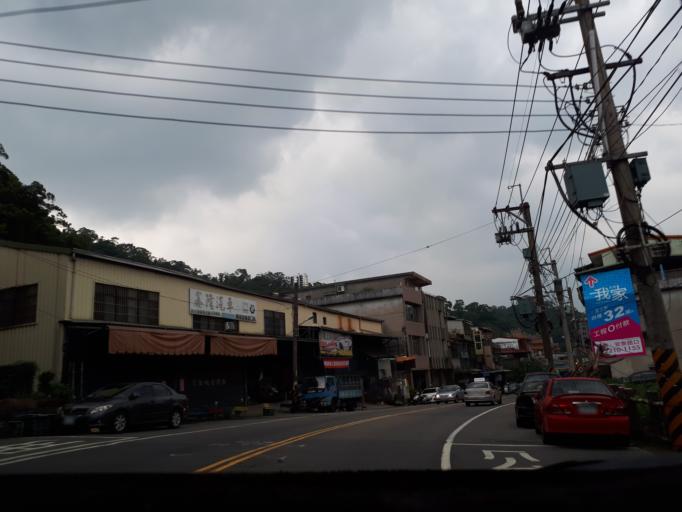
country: TW
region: Taipei
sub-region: Taipei
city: Banqiao
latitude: 24.9512
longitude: 121.4845
